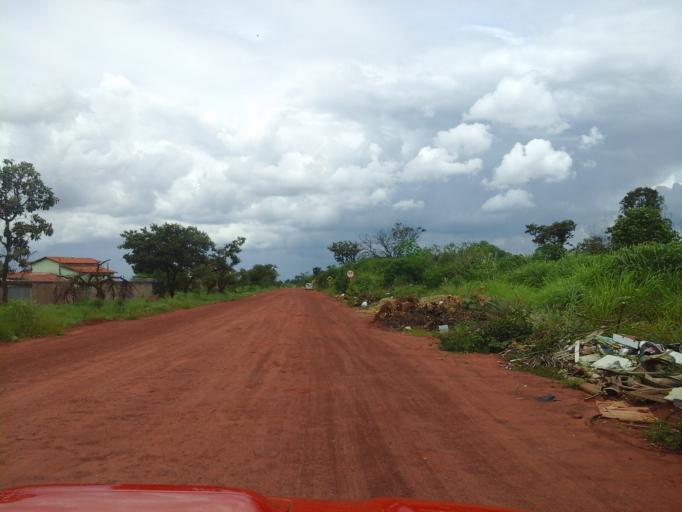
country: BR
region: Federal District
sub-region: Brasilia
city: Brasilia
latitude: -15.6934
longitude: -47.8245
